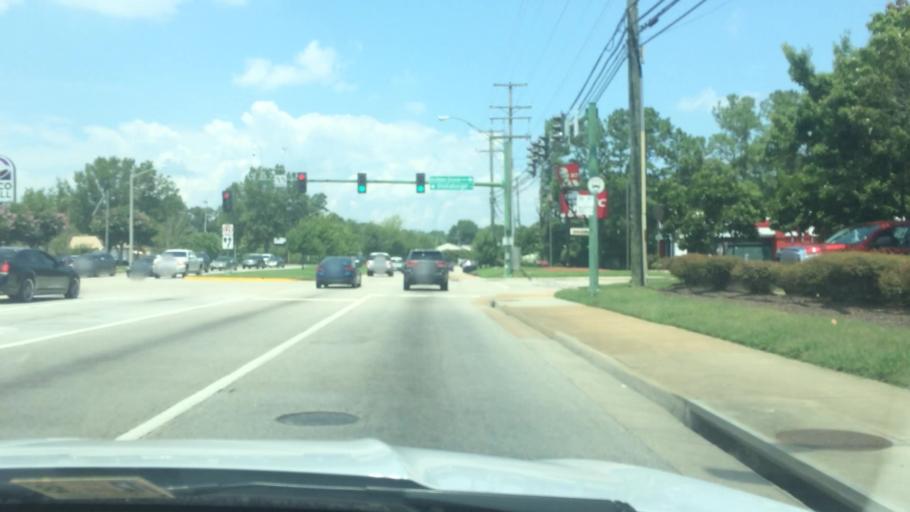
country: US
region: Virginia
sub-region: York County
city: Yorktown
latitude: 37.1580
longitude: -76.5566
